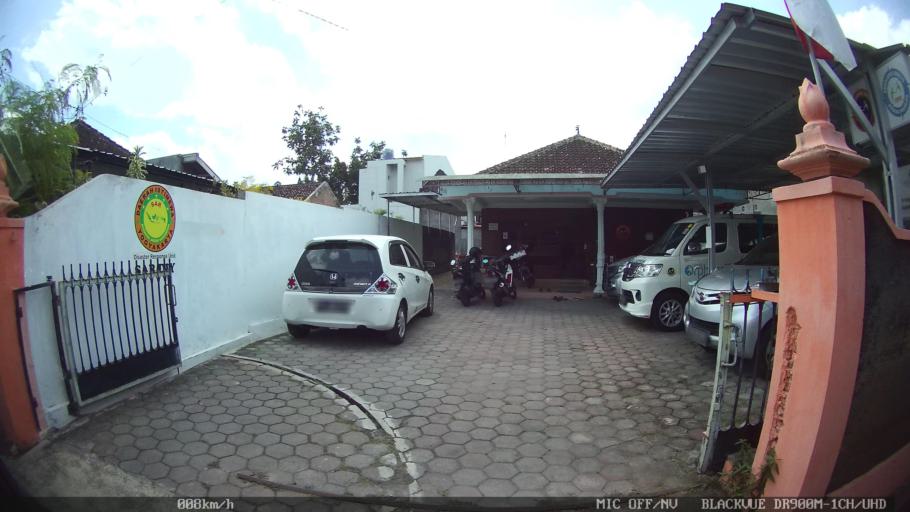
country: ID
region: Daerah Istimewa Yogyakarta
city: Kasihan
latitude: -7.8215
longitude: 110.3521
